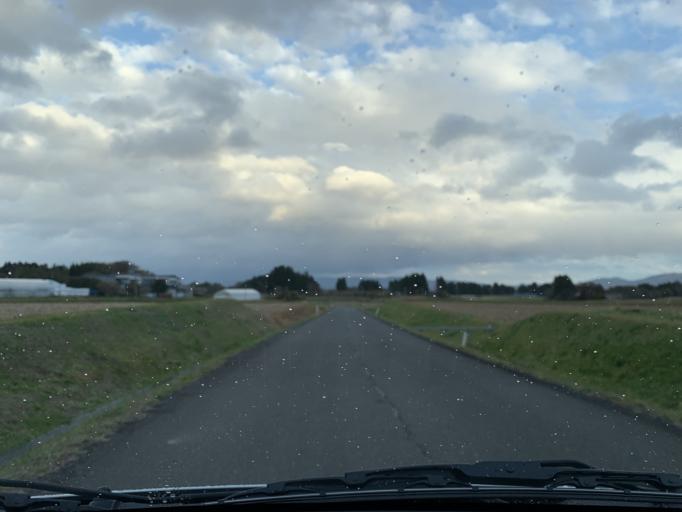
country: JP
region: Iwate
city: Mizusawa
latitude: 39.0755
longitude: 141.0351
